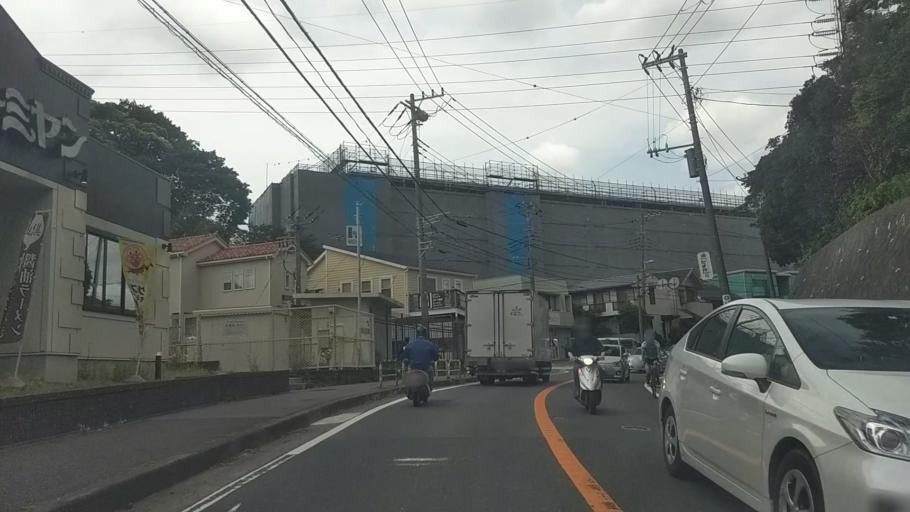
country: JP
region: Kanagawa
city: Fujisawa
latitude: 35.3238
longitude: 139.5064
